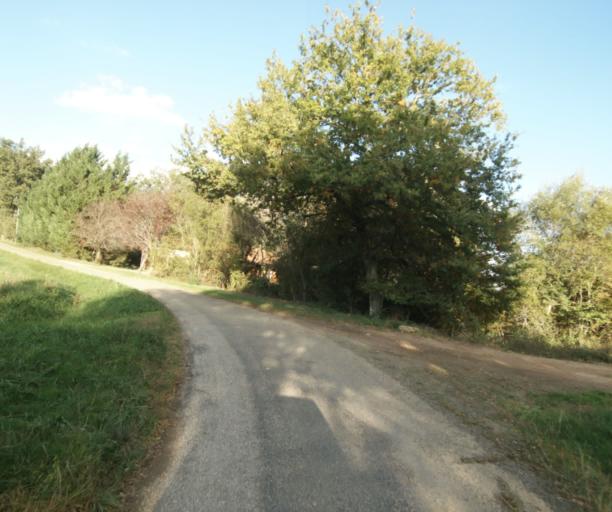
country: FR
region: Midi-Pyrenees
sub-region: Departement du Gers
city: Eauze
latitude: 43.7426
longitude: 0.1130
